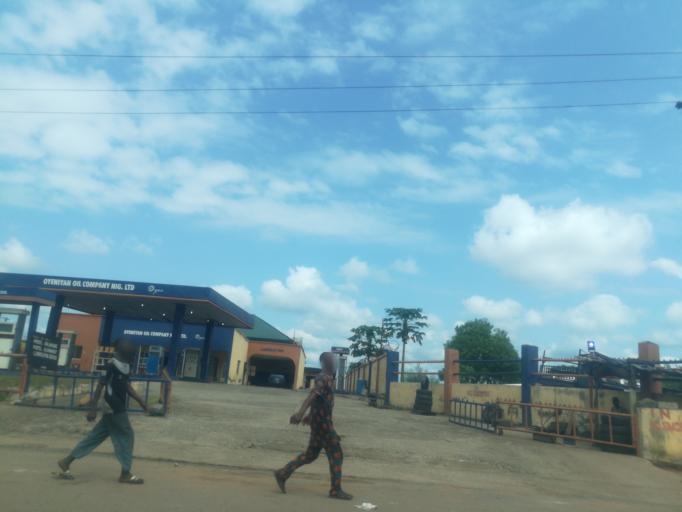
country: NG
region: Oyo
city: Egbeda
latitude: 7.4266
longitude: 3.9949
